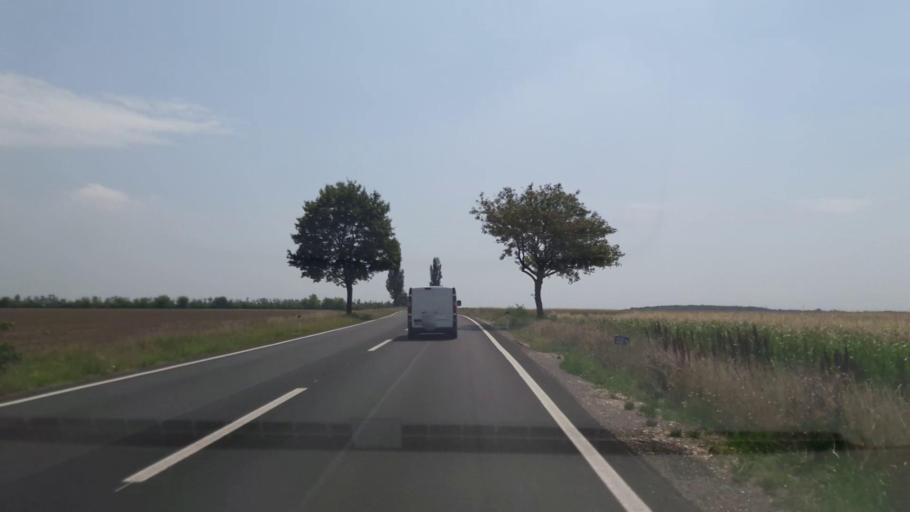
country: AT
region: Lower Austria
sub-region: Politischer Bezirk Wien-Umgebung
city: Rauchenwarth
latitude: 48.0982
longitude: 16.5407
